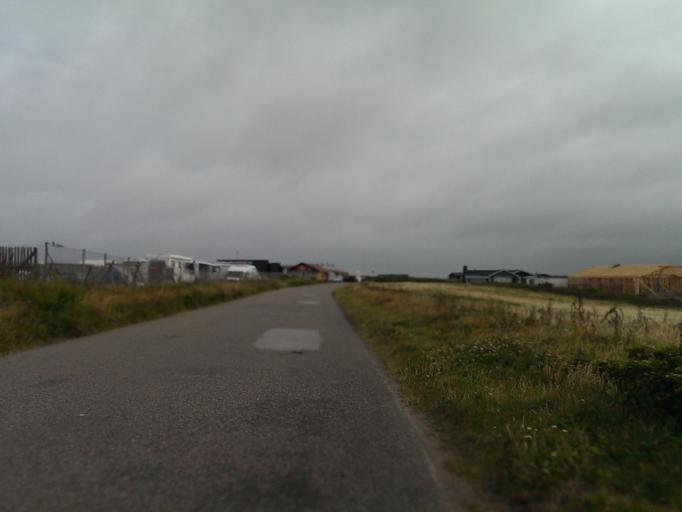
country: DK
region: North Denmark
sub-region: Jammerbugt Kommune
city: Pandrup
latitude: 57.3842
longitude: 9.7255
